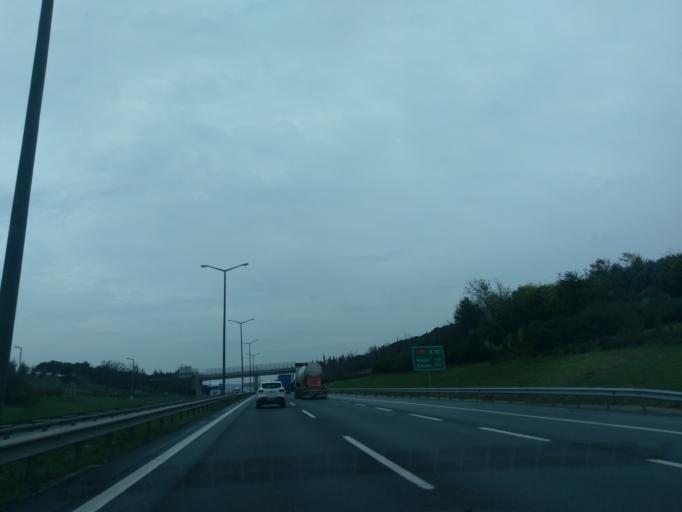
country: TR
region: Istanbul
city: Silivri
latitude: 41.1120
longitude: 28.2639
